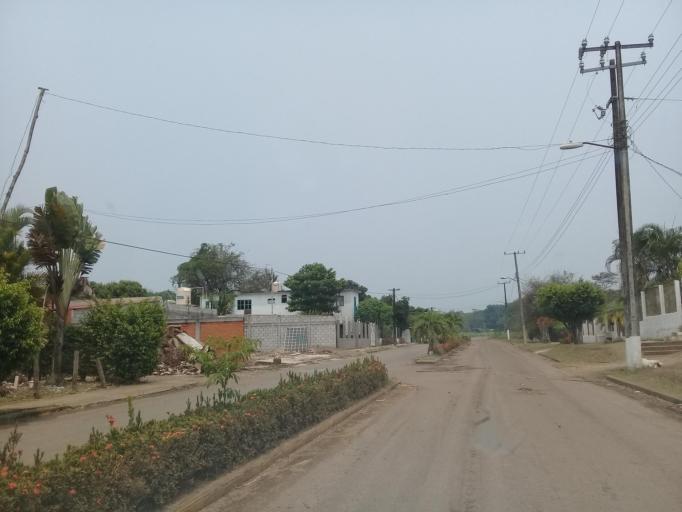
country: MX
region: Veracruz
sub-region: Tezonapa
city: Laguna Chica (Pueblo Nuevo)
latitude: 18.5182
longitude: -96.7227
